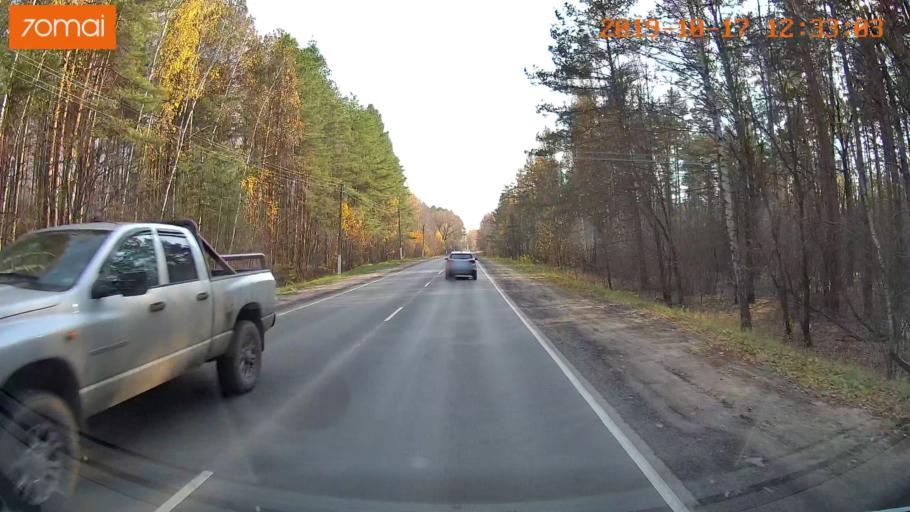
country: RU
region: Rjazan
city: Kasimov
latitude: 54.9578
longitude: 41.3496
